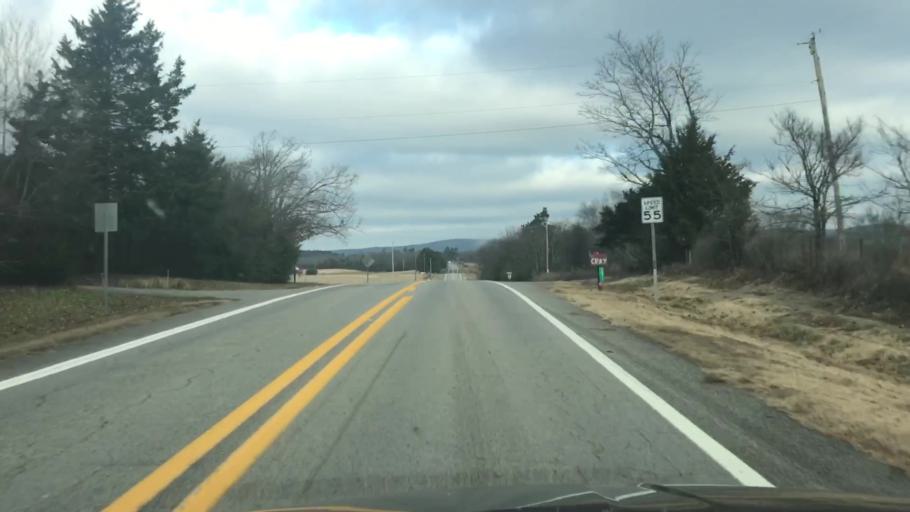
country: US
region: Arkansas
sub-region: Montgomery County
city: Mount Ida
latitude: 34.6354
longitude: -93.7383
